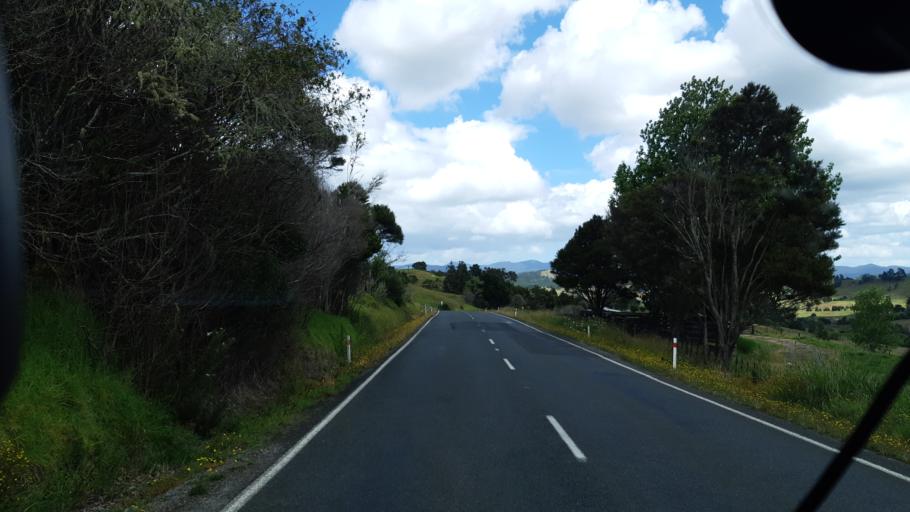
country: NZ
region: Northland
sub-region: Far North District
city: Waimate North
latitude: -35.3013
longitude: 173.5905
